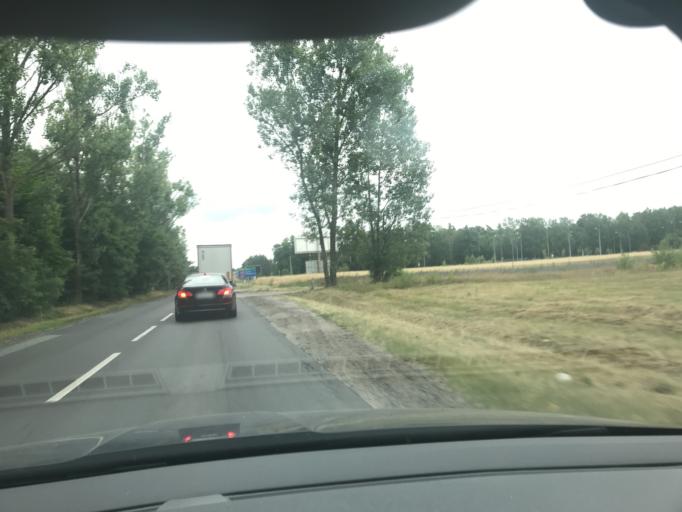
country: PL
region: Lodz Voivodeship
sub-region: Powiat zgierski
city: Zgierz
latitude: 51.9088
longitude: 19.4314
